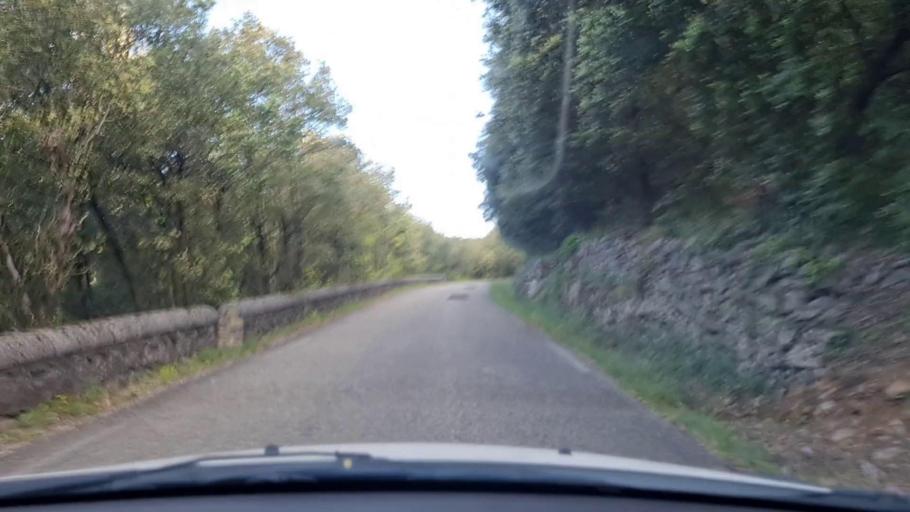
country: FR
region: Languedoc-Roussillon
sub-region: Departement du Gard
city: Cendras
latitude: 44.1607
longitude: 4.0284
